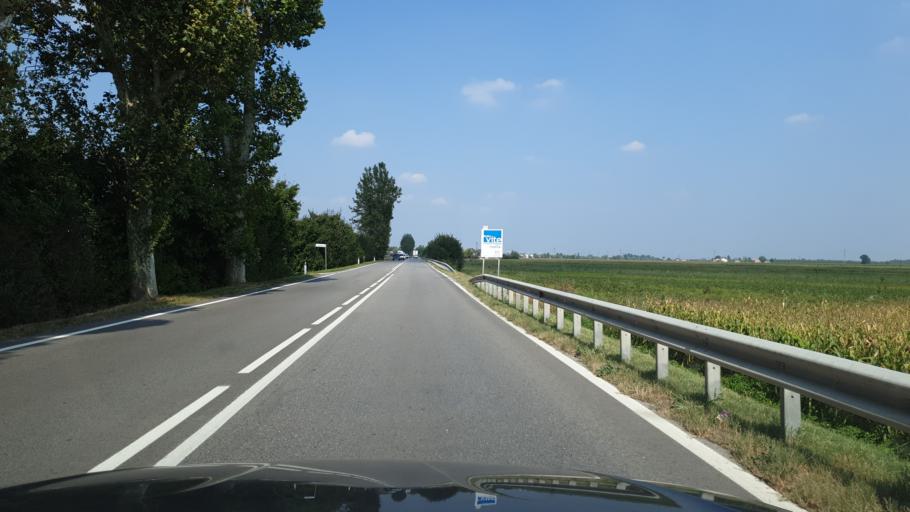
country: IT
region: Veneto
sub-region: Provincia di Rovigo
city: Bosaro
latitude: 45.0150
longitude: 11.7690
